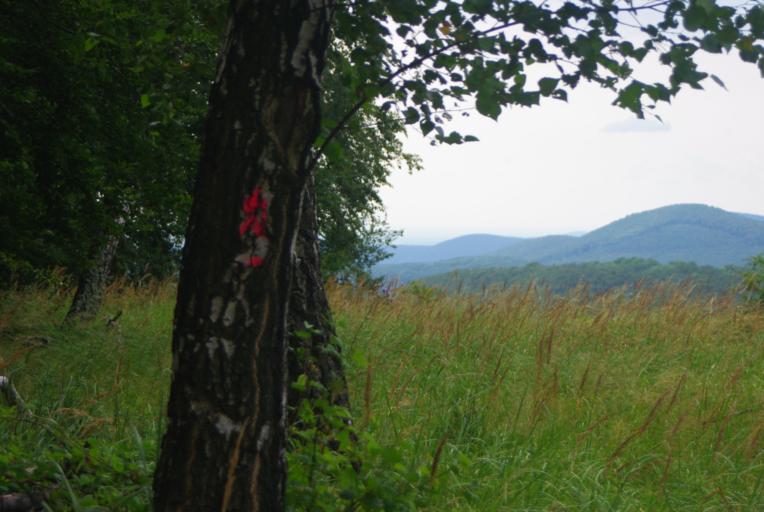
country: HU
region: Borsod-Abauj-Zemplen
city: Gonc
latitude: 48.4147
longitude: 21.3807
